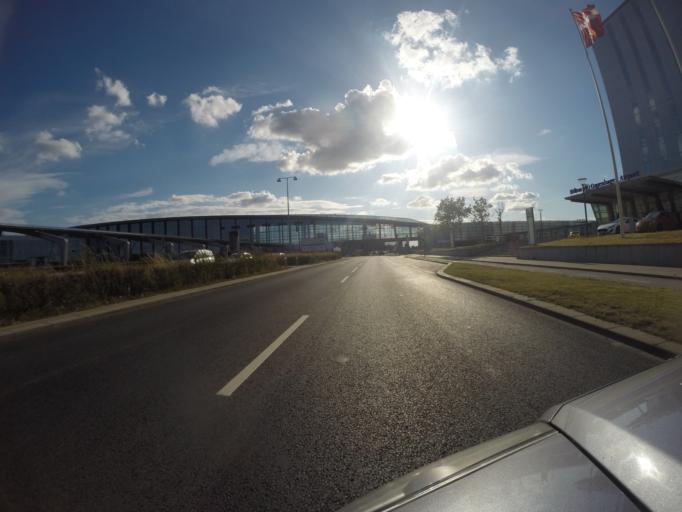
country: DK
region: Capital Region
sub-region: Dragor Kommune
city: Dragor
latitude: 55.6299
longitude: 12.6513
